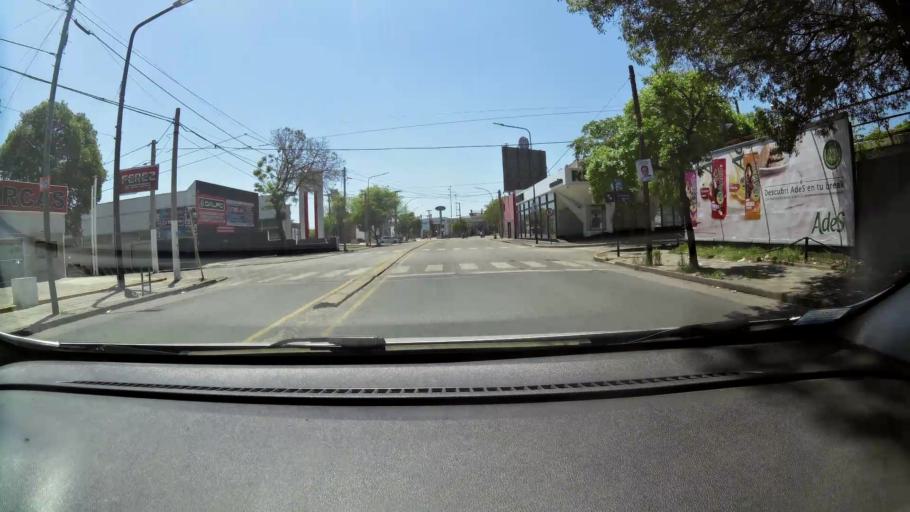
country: AR
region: Cordoba
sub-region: Departamento de Capital
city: Cordoba
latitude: -31.3918
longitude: -64.2033
